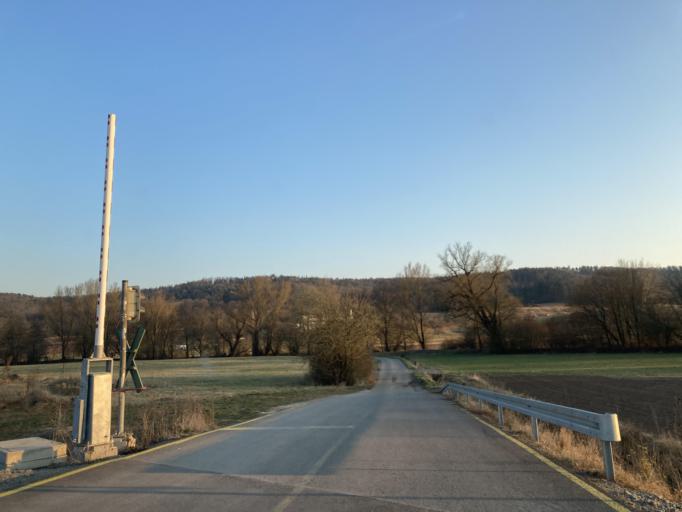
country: DE
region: Baden-Wuerttemberg
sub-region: Tuebingen Region
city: Tuebingen
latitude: 48.5214
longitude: 8.9989
